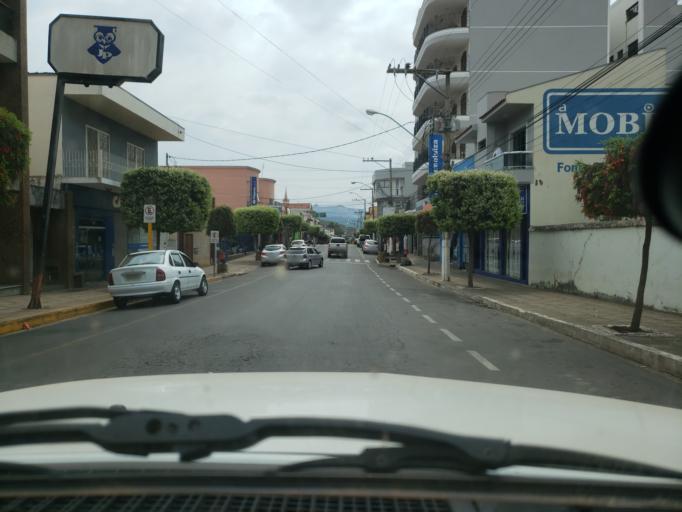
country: BR
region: Minas Gerais
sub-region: Jacutinga
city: Jacutinga
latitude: -22.2898
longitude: -46.6133
